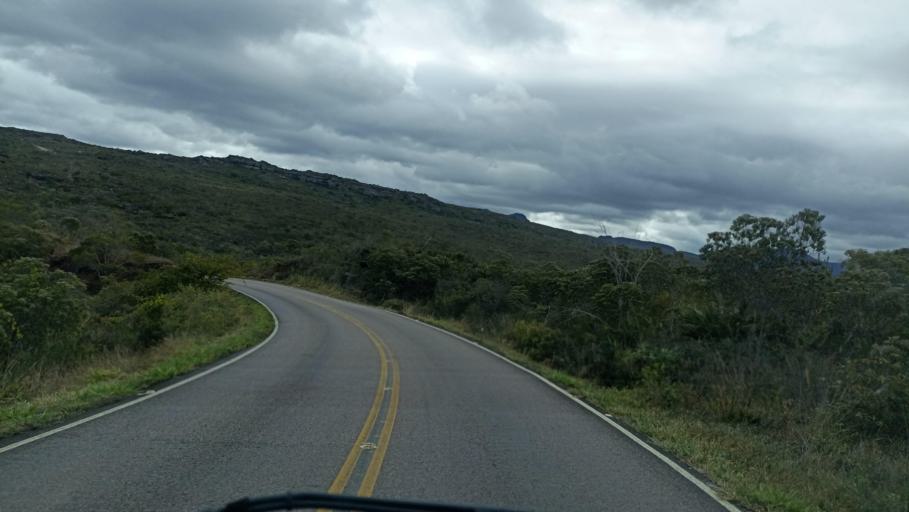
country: BR
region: Bahia
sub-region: Andarai
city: Vera Cruz
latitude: -12.9899
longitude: -41.3485
